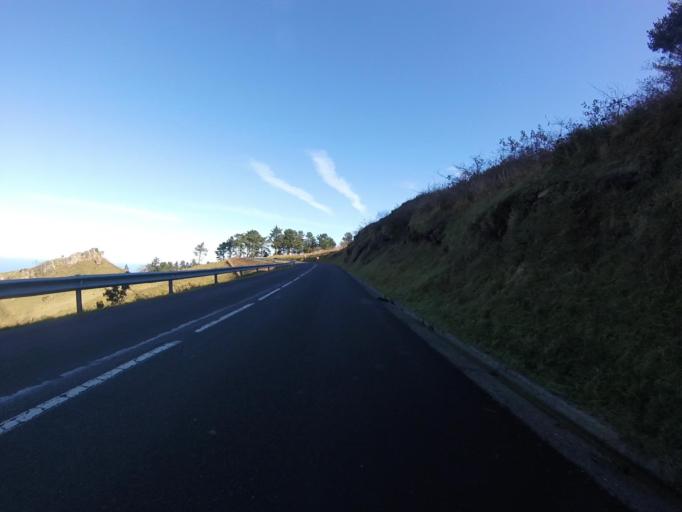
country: ES
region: Basque Country
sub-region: Provincia de Guipuzcoa
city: Lezo
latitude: 43.3465
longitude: -1.8594
